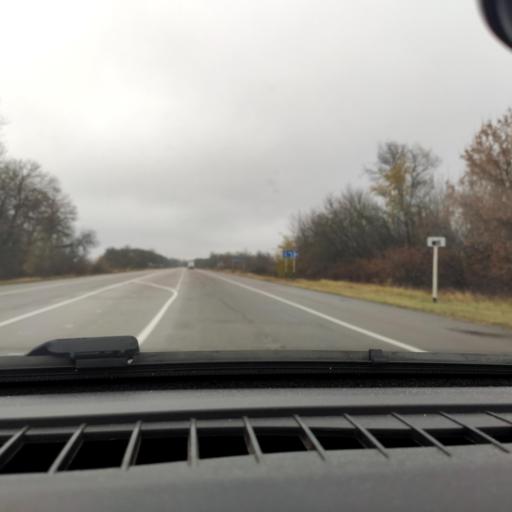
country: RU
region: Voronezj
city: Kolodeznyy
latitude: 51.3088
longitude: 39.0364
